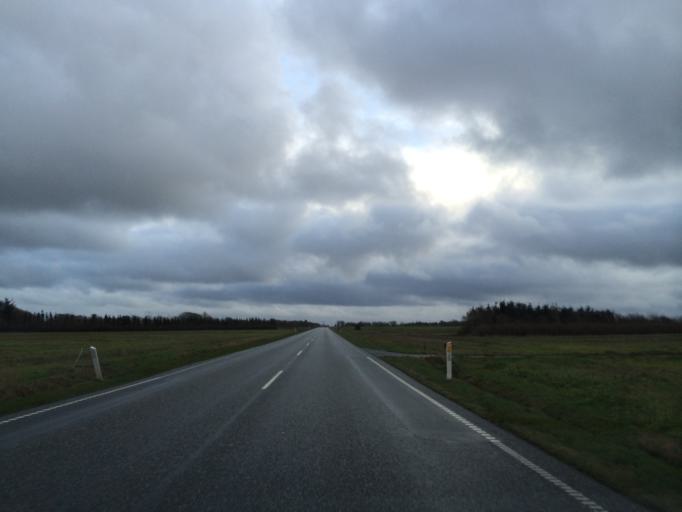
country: DK
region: Central Jutland
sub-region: Ringkobing-Skjern Kommune
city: Ringkobing
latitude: 56.1008
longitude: 8.3298
